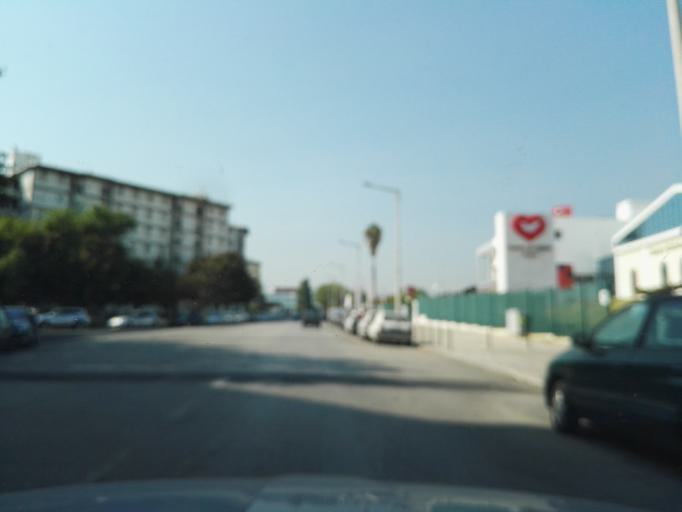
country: PT
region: Lisbon
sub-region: Loures
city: Moscavide
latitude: 38.7548
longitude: -9.1104
